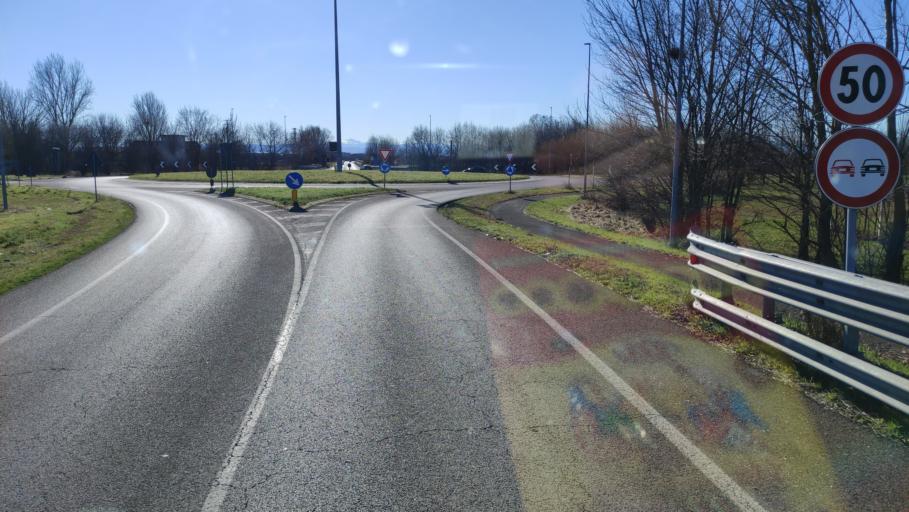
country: IT
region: Emilia-Romagna
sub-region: Provincia di Reggio Emilia
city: San Martino in Rio
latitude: 44.7347
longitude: 10.7666
